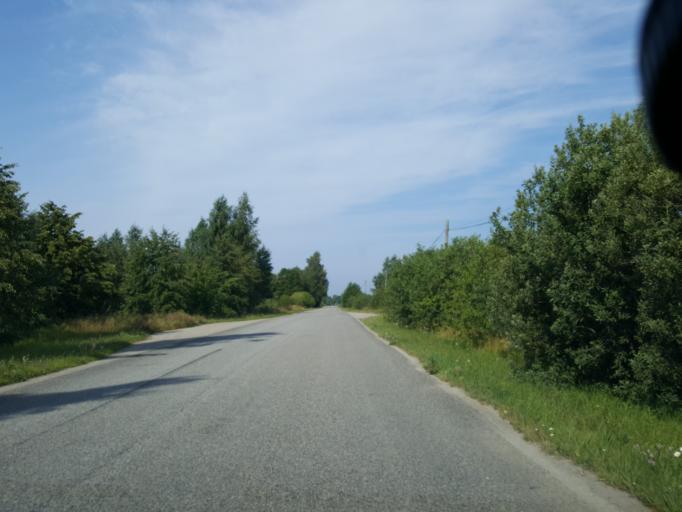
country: LV
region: Salacgrivas
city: Salacgriva
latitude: 57.7550
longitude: 24.3890
